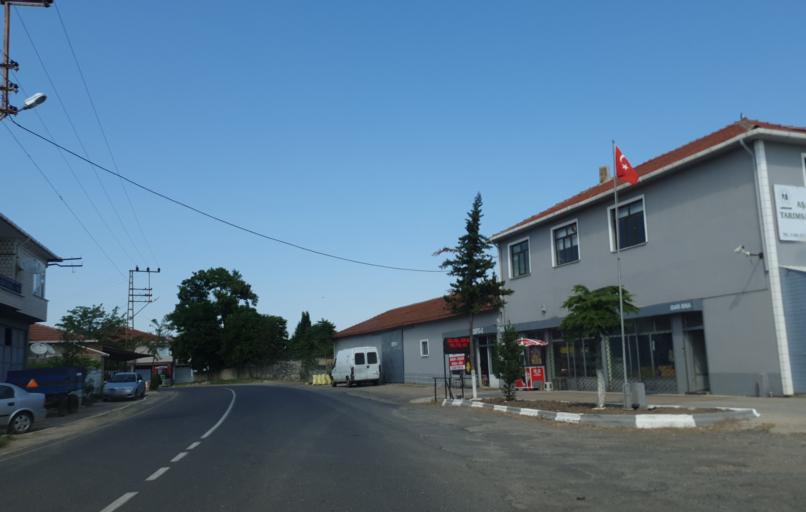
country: TR
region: Tekirdag
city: Muratli
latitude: 41.2188
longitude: 27.5436
